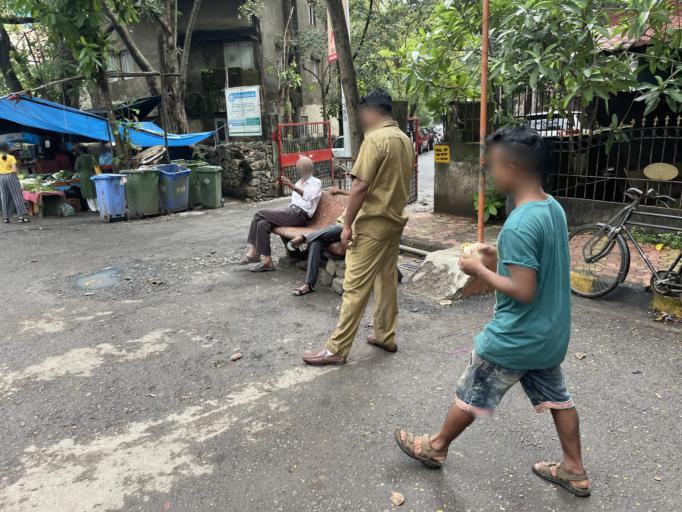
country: IN
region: Maharashtra
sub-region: Mumbai Suburban
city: Borivli
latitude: 19.2294
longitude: 72.8649
